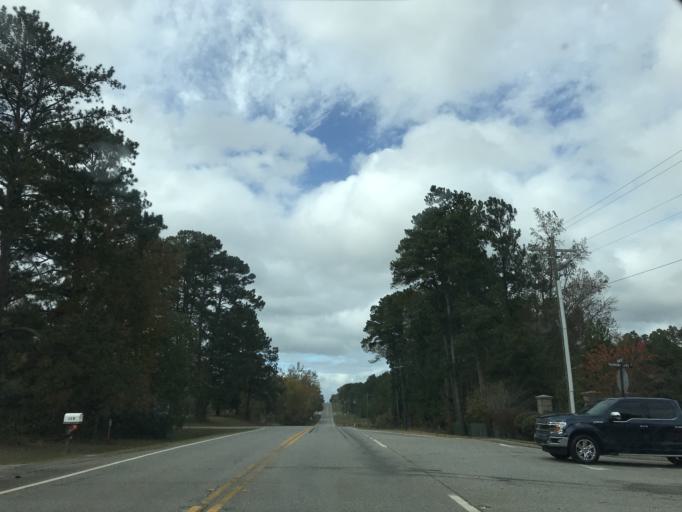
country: US
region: Georgia
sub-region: Jones County
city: Gray
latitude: 32.9867
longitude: -83.5153
